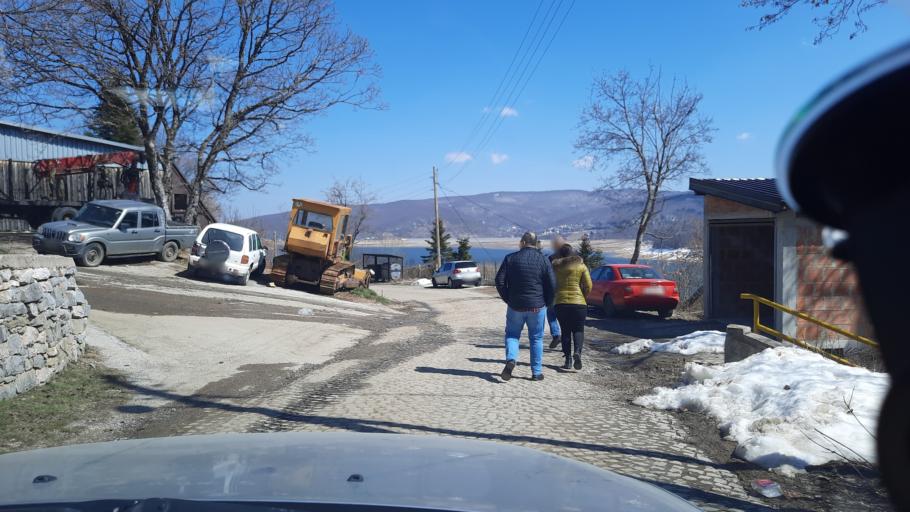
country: MK
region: Gostivar
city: Vrutok
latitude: 41.7022
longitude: 20.7564
